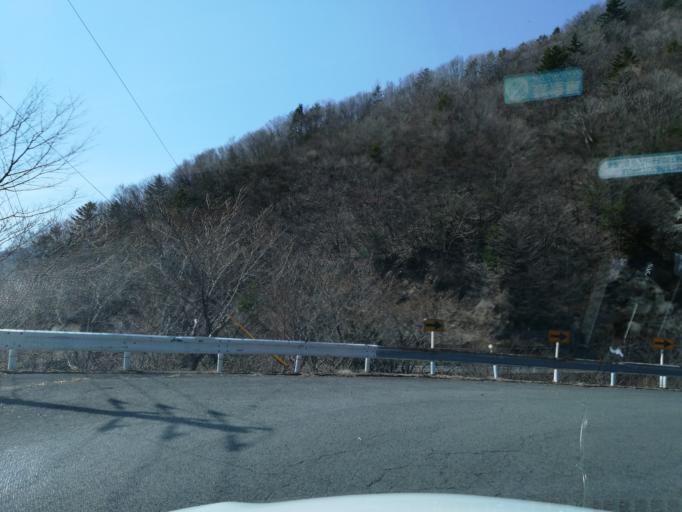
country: JP
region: Tokushima
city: Wakimachi
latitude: 33.8666
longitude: 134.0785
